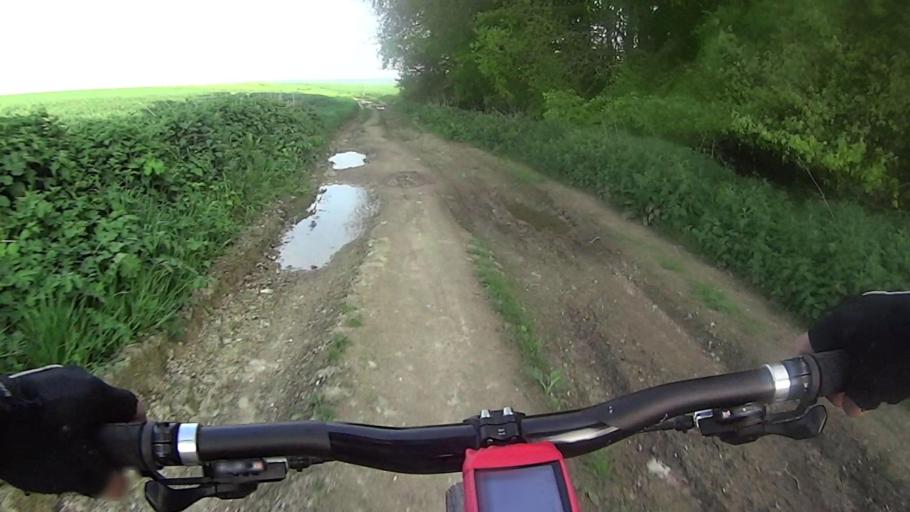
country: GB
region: England
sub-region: West Sussex
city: Arundel
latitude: 50.8992
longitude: -0.5789
